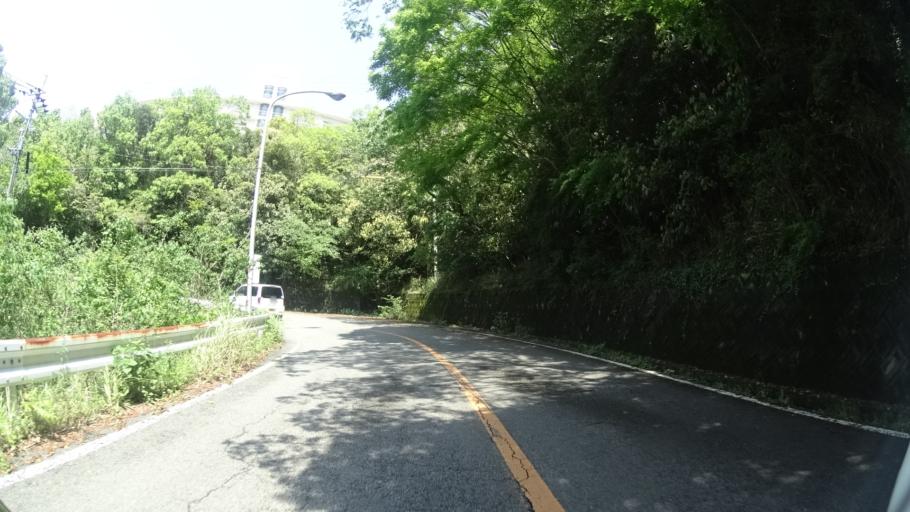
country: JP
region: Tokushima
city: Tokushima-shi
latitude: 34.0662
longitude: 134.5316
